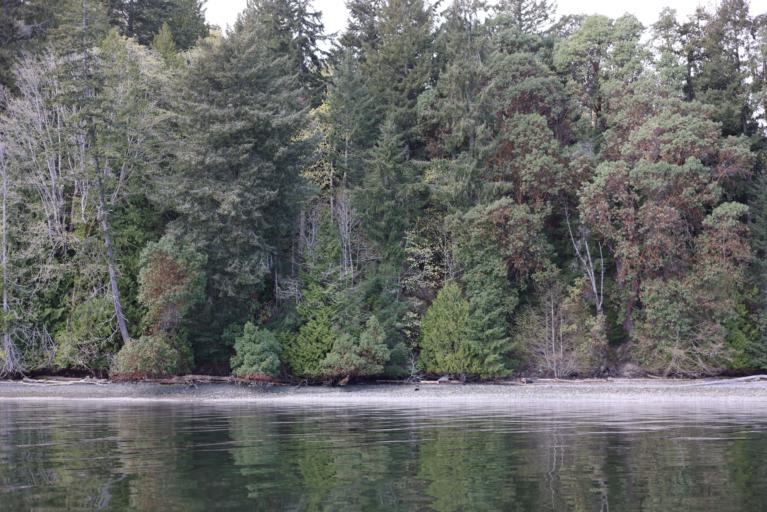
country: CA
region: British Columbia
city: North Saanich
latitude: 48.6003
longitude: -123.5213
